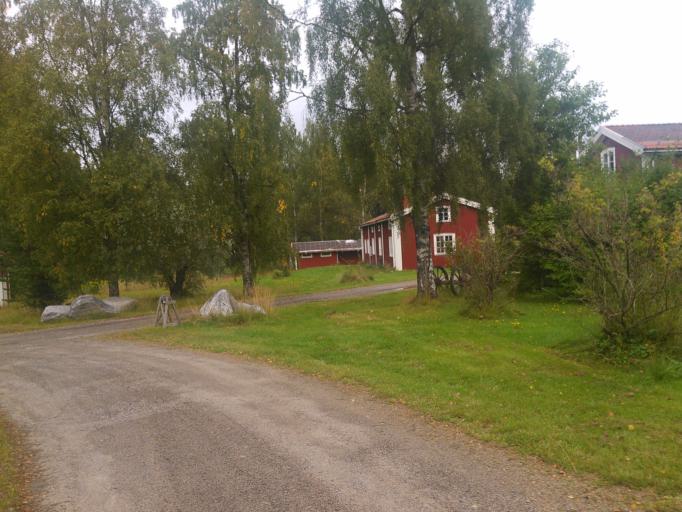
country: SE
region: Vaesterbotten
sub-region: Umea Kommun
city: Ersmark
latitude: 63.9306
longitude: 20.3848
